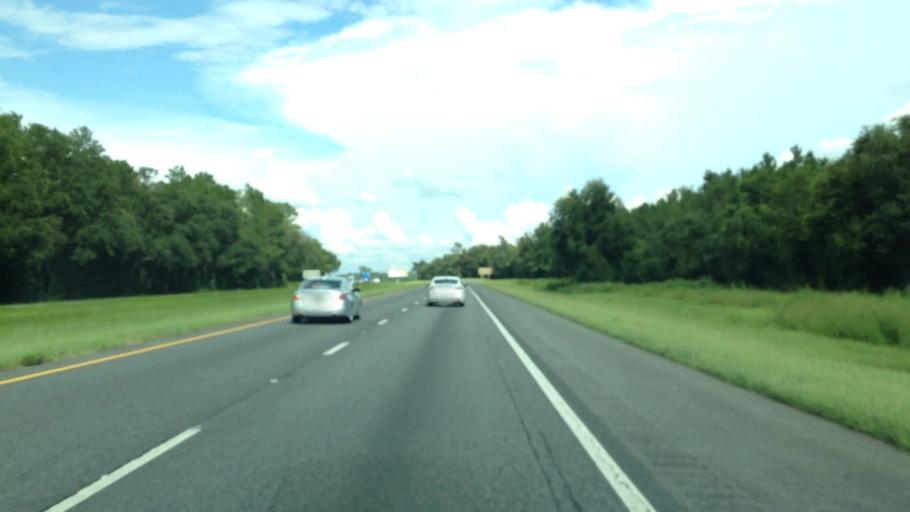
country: US
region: Florida
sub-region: Suwannee County
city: Live Oak
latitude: 30.3381
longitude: -83.1114
